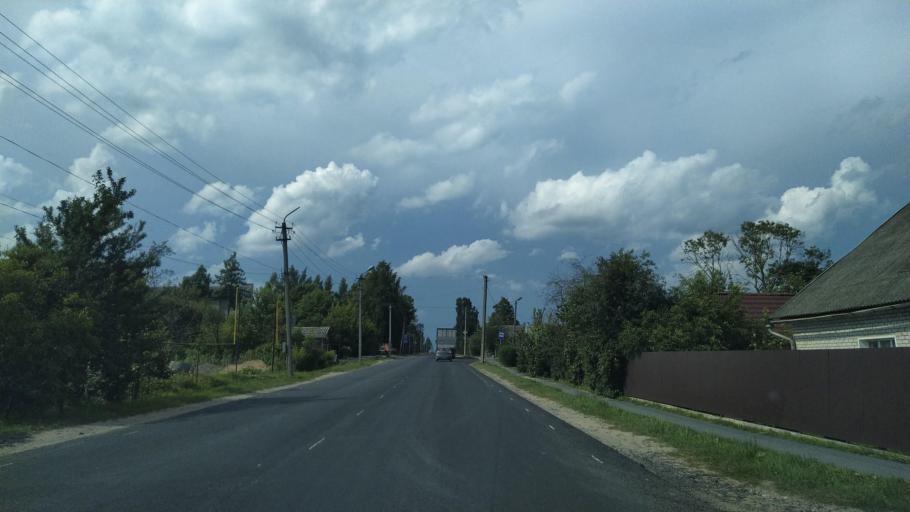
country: RU
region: Pskov
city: Porkhov
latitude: 57.7758
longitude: 29.5459
